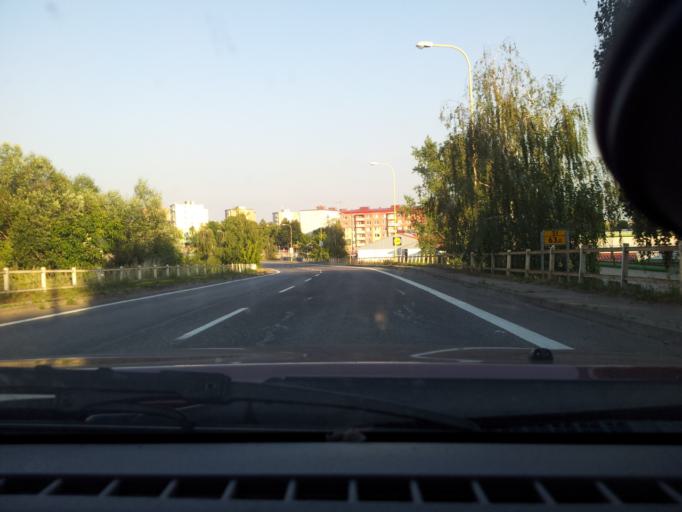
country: SK
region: Trnavsky
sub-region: Okres Skalica
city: Holic
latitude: 48.8160
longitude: 17.1527
